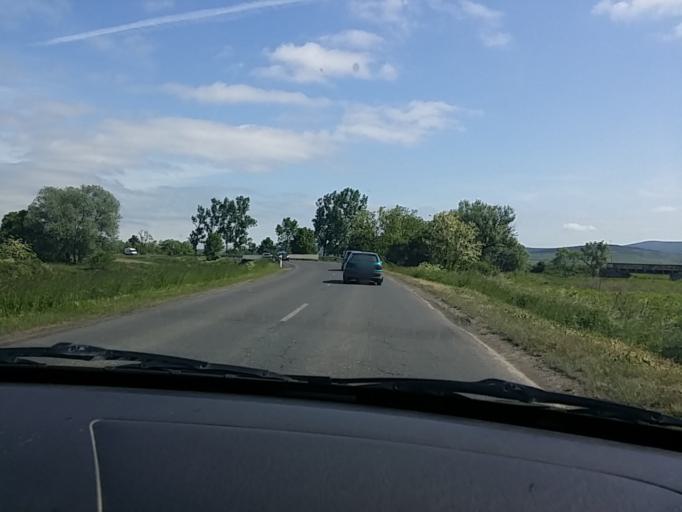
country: HU
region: Borsod-Abauj-Zemplen
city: Satoraljaujhely
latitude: 48.4426
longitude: 21.6251
